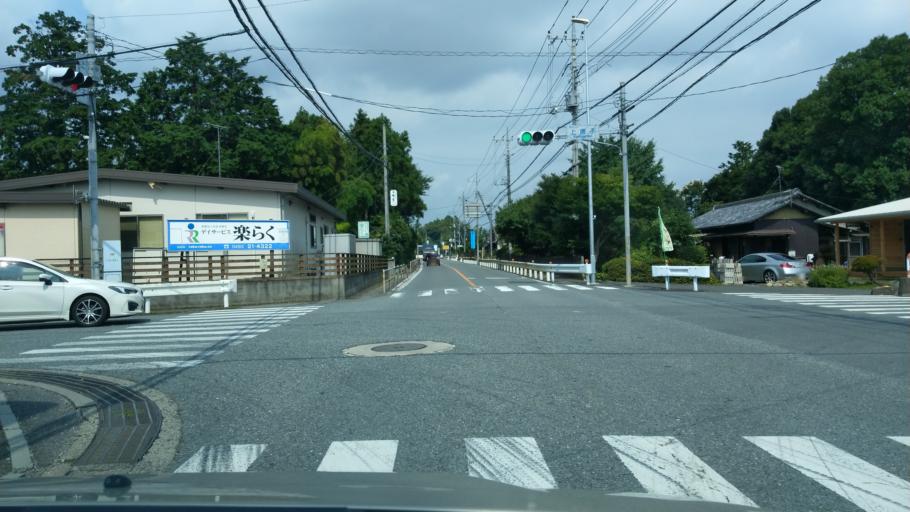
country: JP
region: Saitama
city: Ogawa
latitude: 36.0349
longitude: 139.3421
